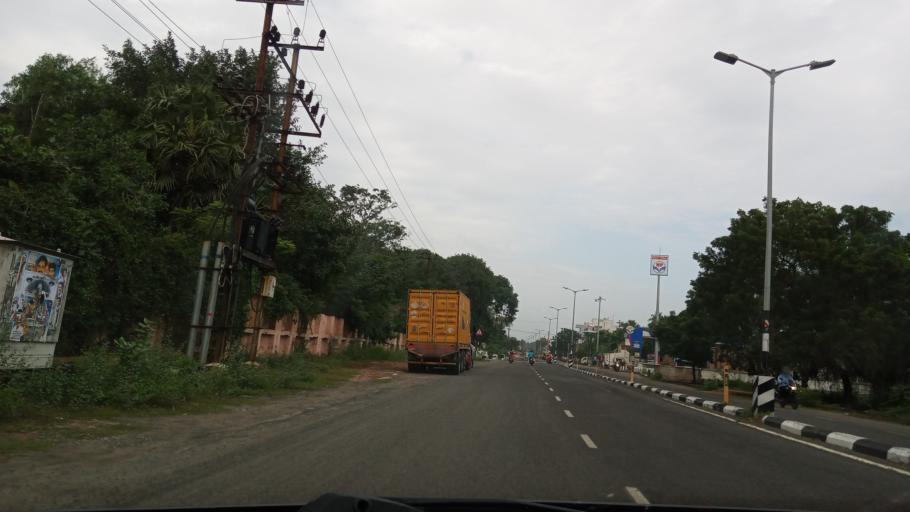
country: IN
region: Tamil Nadu
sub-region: Villupuram
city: Auroville
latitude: 12.0180
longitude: 79.8593
